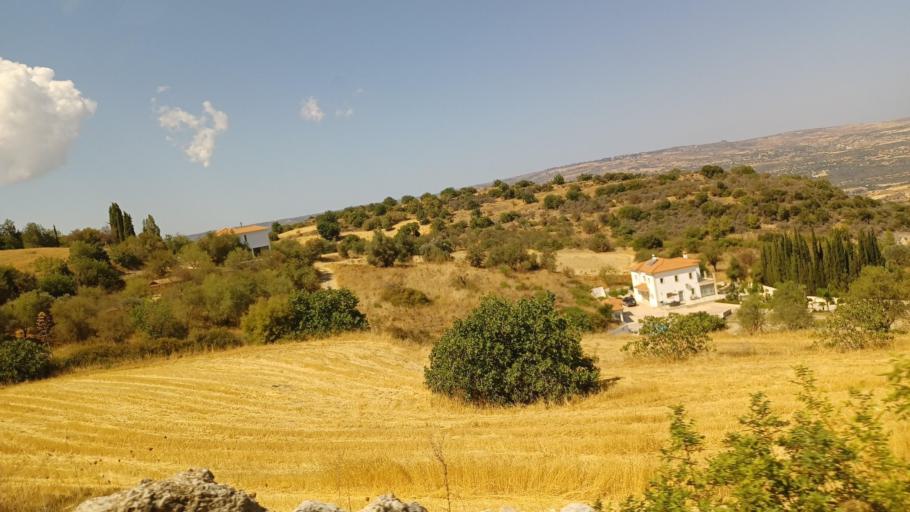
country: CY
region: Pafos
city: Polis
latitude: 34.9843
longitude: 32.4905
